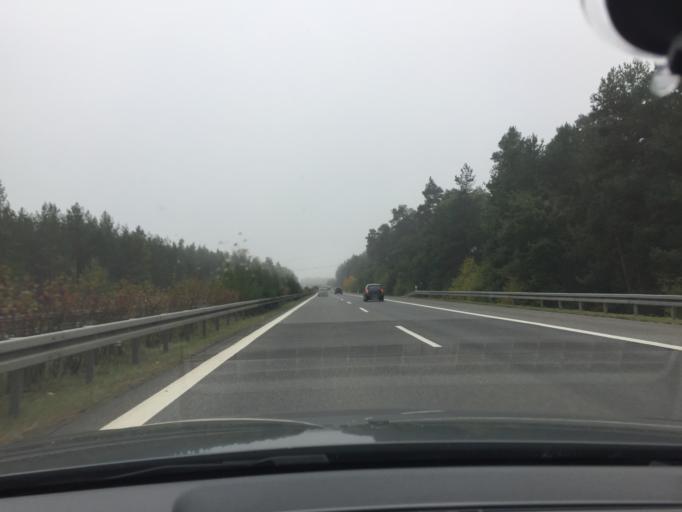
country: DE
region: Brandenburg
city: Bronkow
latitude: 51.6411
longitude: 13.9421
